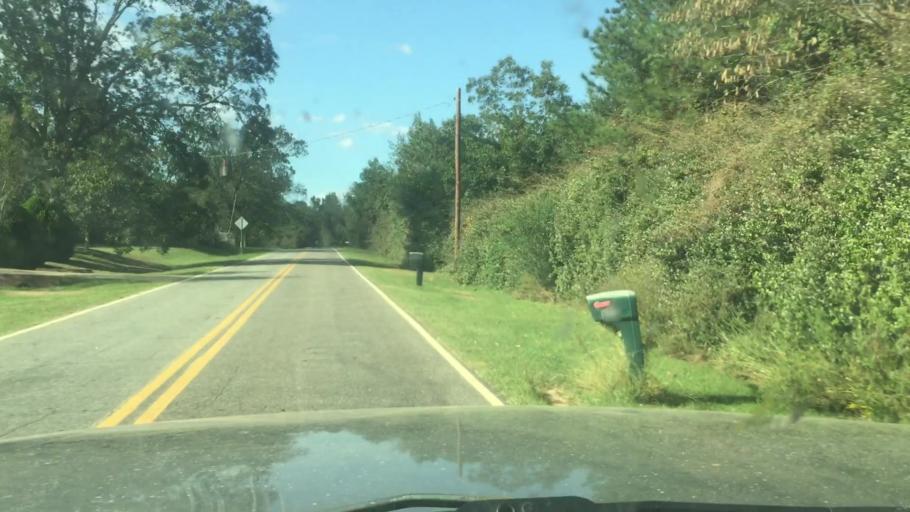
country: US
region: Georgia
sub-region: Terrell County
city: Dawson
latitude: 31.7329
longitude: -84.3419
